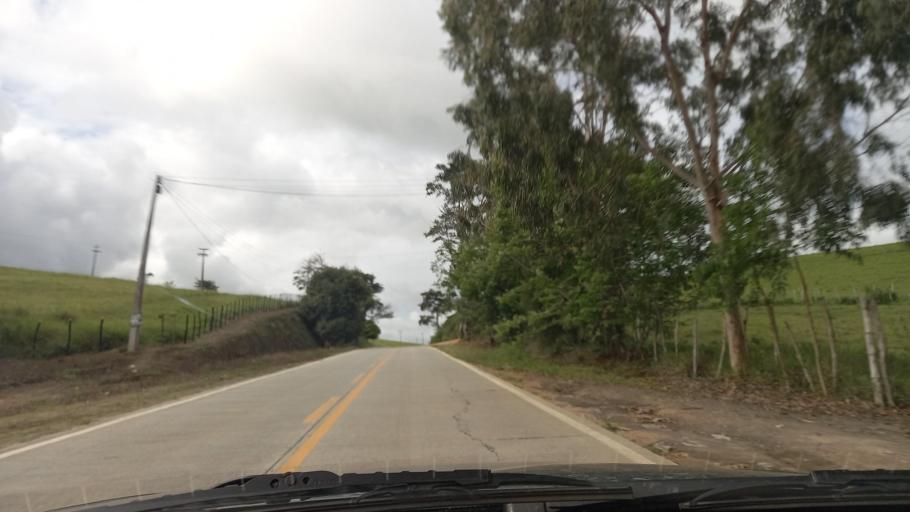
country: BR
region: Pernambuco
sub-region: Quipapa
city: Quipapa
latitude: -8.7775
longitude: -35.9322
